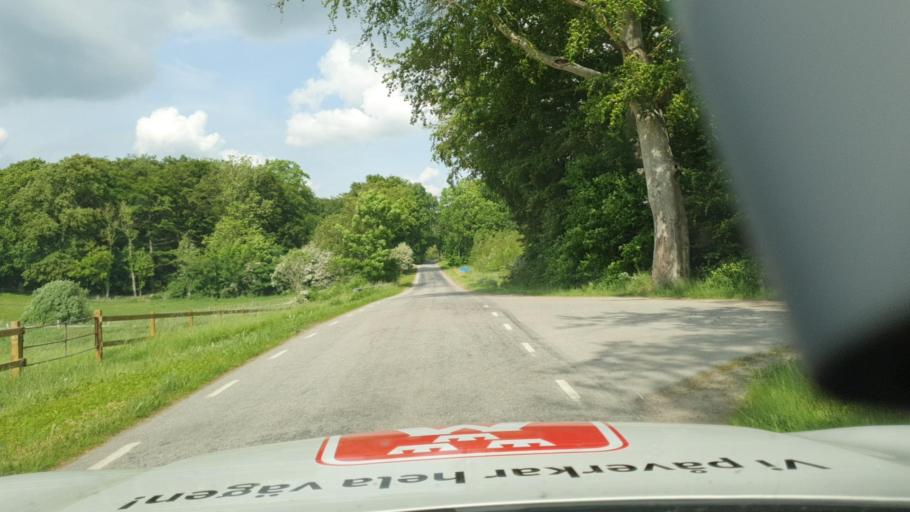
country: SE
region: Skane
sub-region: Skurups Kommun
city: Skurup
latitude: 55.5101
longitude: 13.4975
